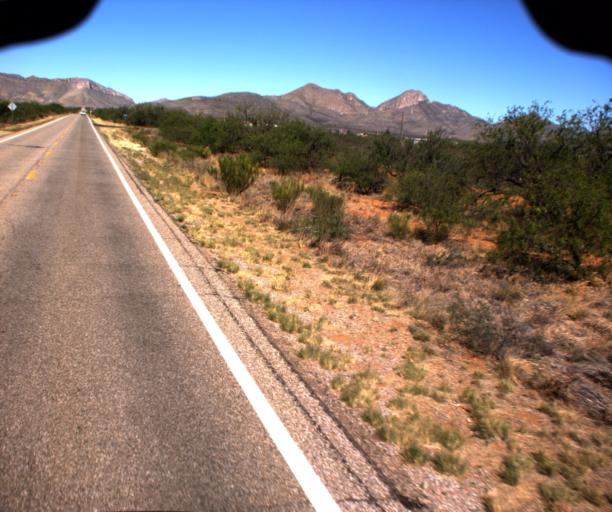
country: US
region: Arizona
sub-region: Cochise County
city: Huachuca City
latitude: 31.6925
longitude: -110.3625
